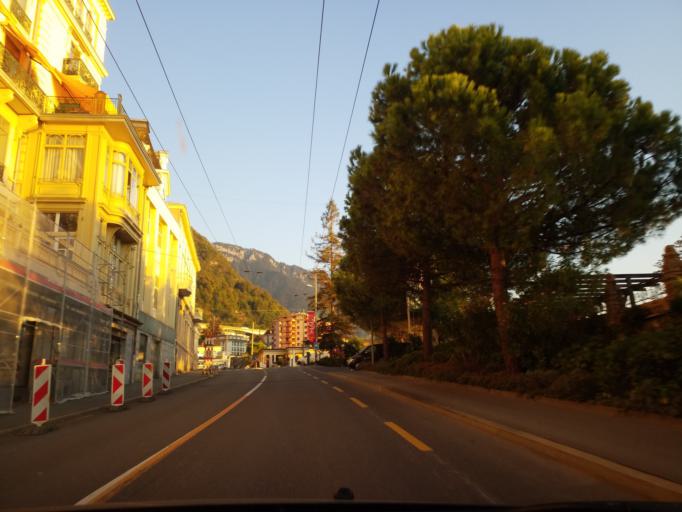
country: CH
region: Vaud
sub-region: Riviera-Pays-d'Enhaut District
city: Montreux
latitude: 46.4256
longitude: 6.9236
